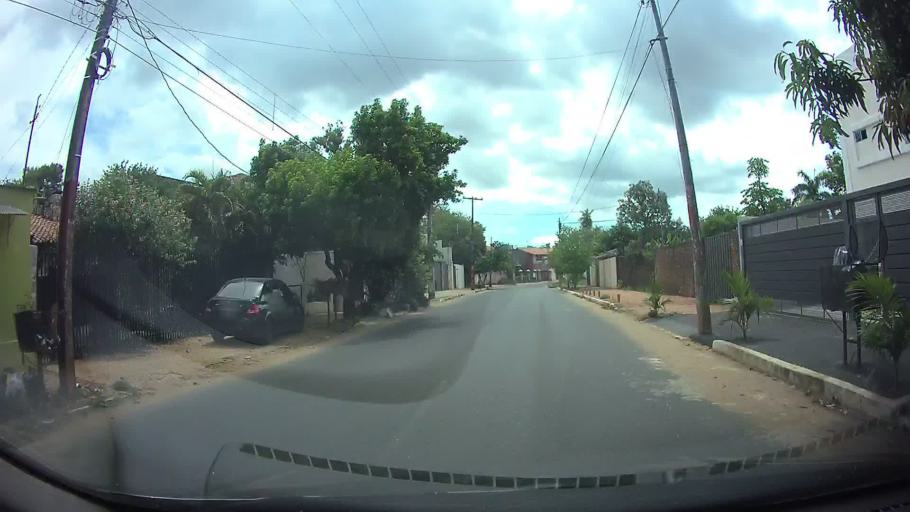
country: PY
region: Central
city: Fernando de la Mora
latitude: -25.3245
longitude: -57.5326
